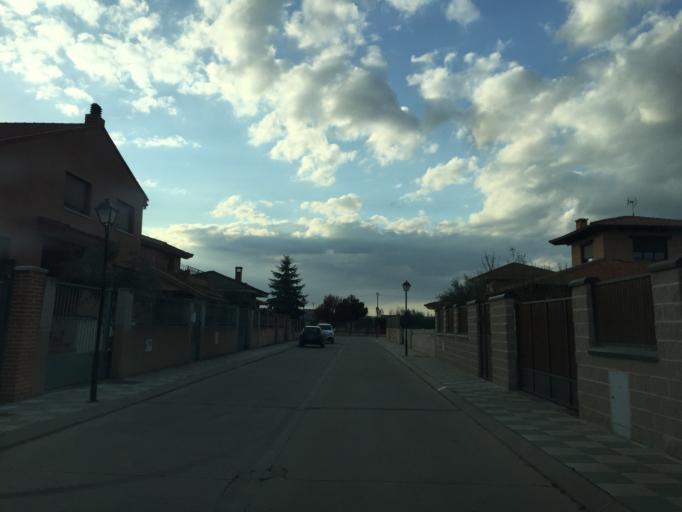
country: ES
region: Castille and Leon
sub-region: Provincia de Palencia
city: Venta de Banos
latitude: 41.9213
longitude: -4.4793
